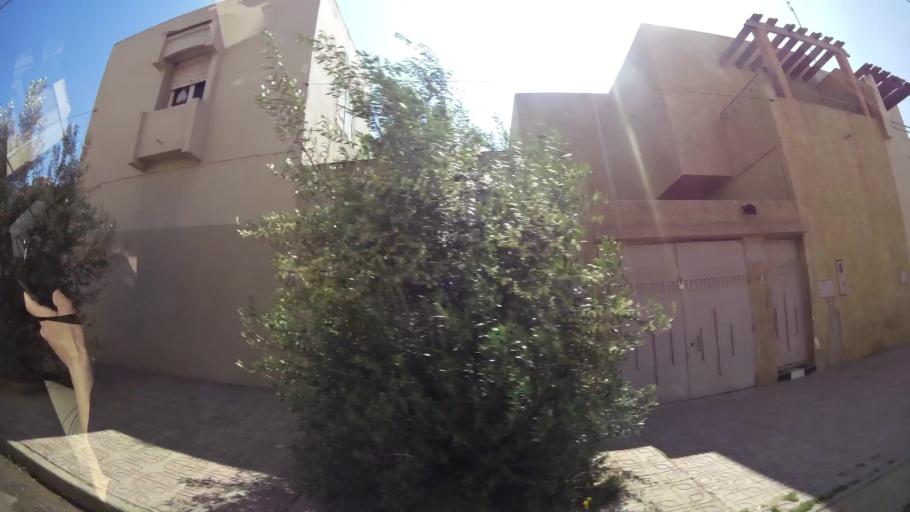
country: MA
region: Oriental
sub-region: Oujda-Angad
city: Oujda
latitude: 34.6924
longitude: -1.8782
